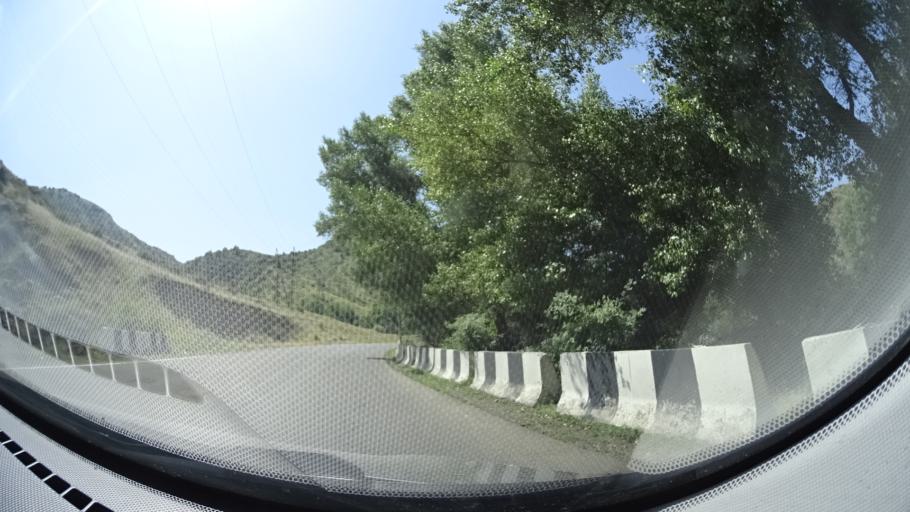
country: GE
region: Samtskhe-Javakheti
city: Aspindza
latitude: 41.5609
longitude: 43.2726
